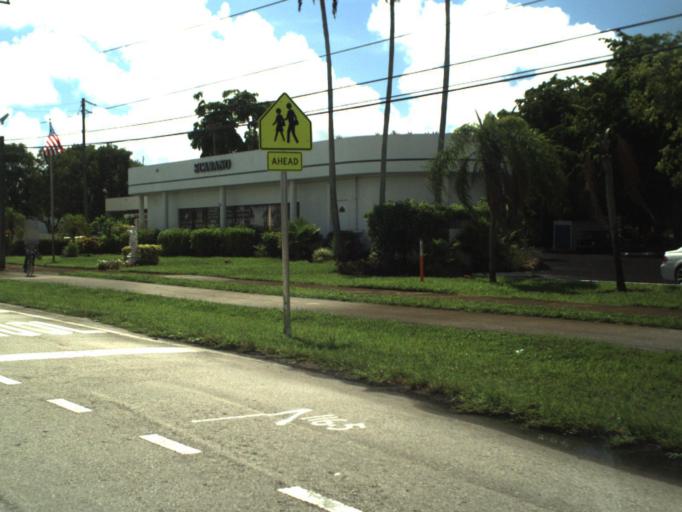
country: US
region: Florida
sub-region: Broward County
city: Miramar
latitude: 26.0085
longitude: -80.2652
